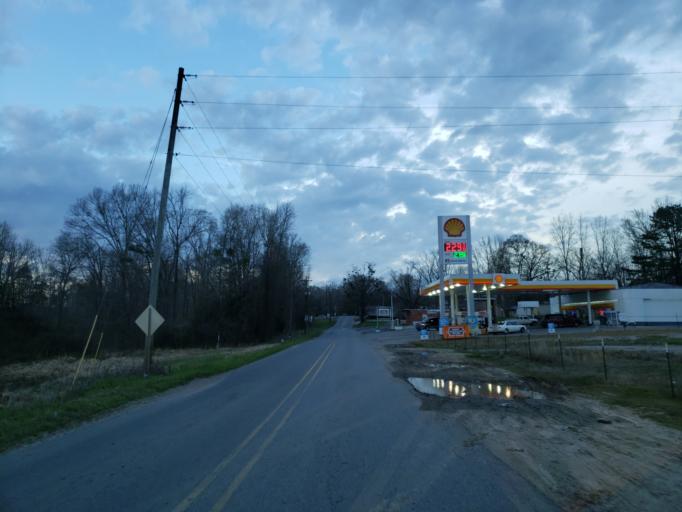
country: US
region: Mississippi
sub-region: Lauderdale County
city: Marion
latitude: 32.4151
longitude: -88.5062
